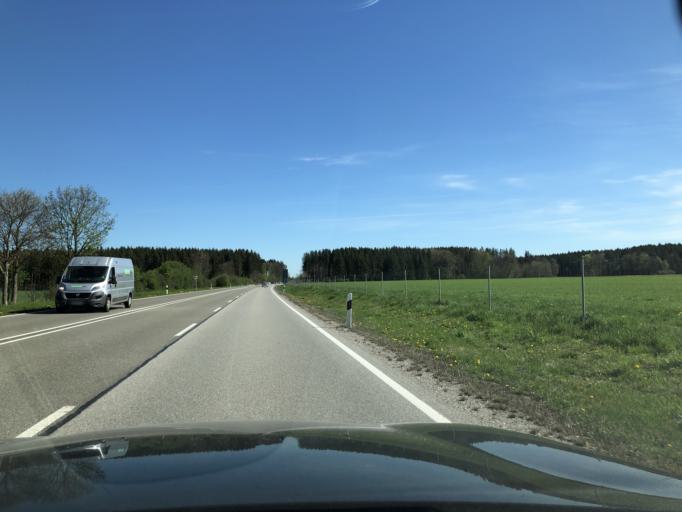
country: DE
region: Bavaria
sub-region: Swabia
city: Jengen
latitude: 47.9774
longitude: 10.6910
